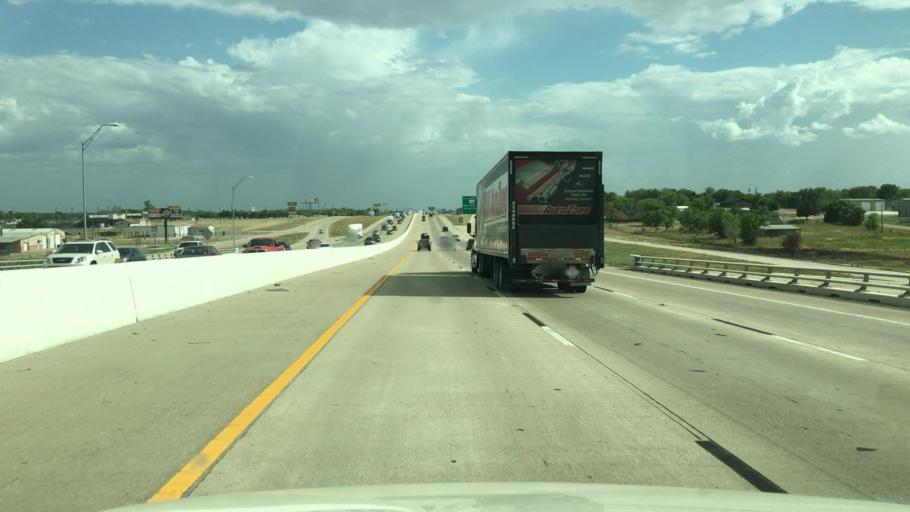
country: US
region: Texas
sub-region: McLennan County
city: Northcrest
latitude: 31.6863
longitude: -97.1000
